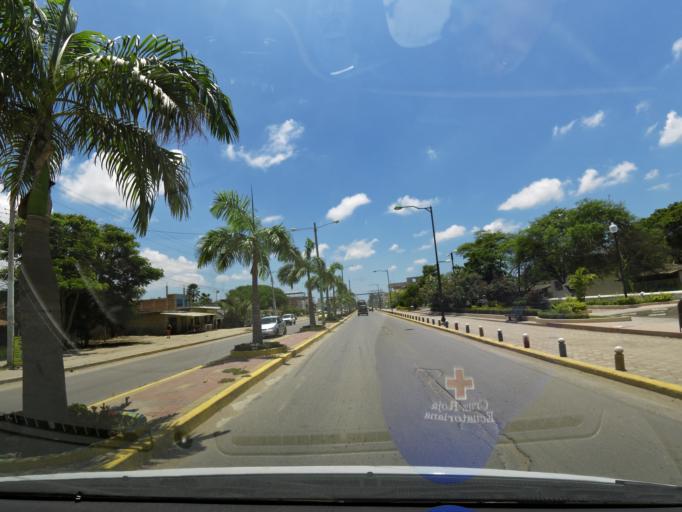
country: EC
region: El Oro
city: Huaquillas
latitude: -3.4833
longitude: -80.2206
